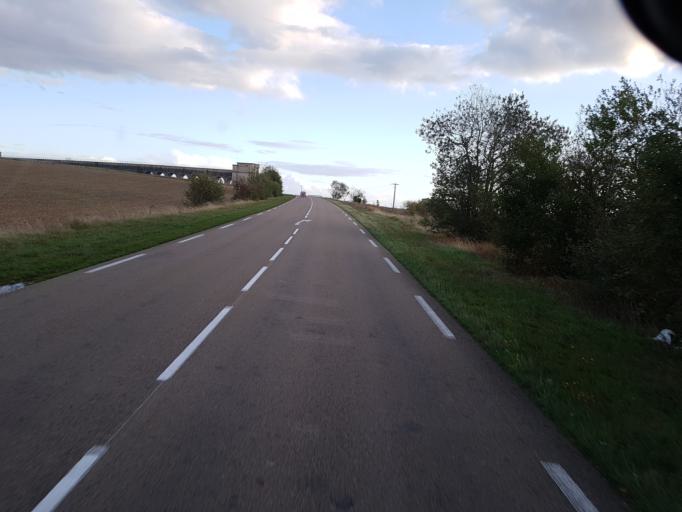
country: FR
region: Bourgogne
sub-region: Departement de l'Yonne
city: Soucy
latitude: 48.2749
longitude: 3.2725
